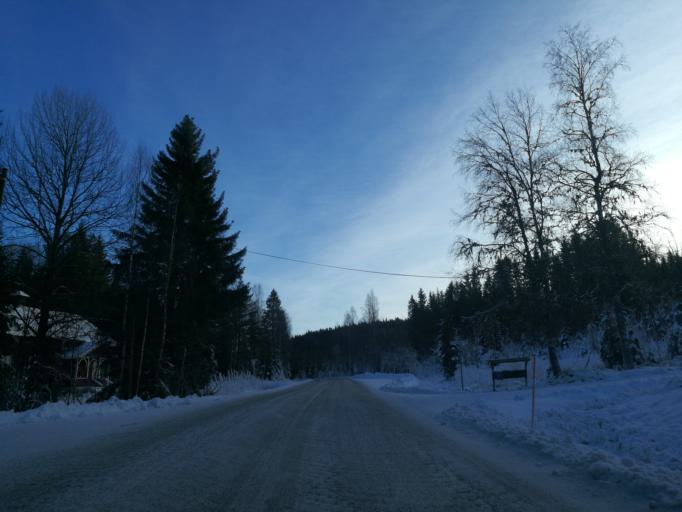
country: NO
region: Hedmark
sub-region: Grue
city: Kirkenaer
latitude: 60.4196
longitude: 12.4250
